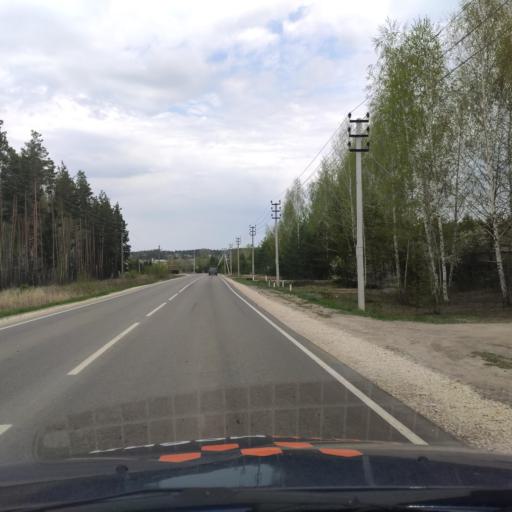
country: RU
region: Voronezj
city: Podgornoye
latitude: 51.8645
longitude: 39.1695
